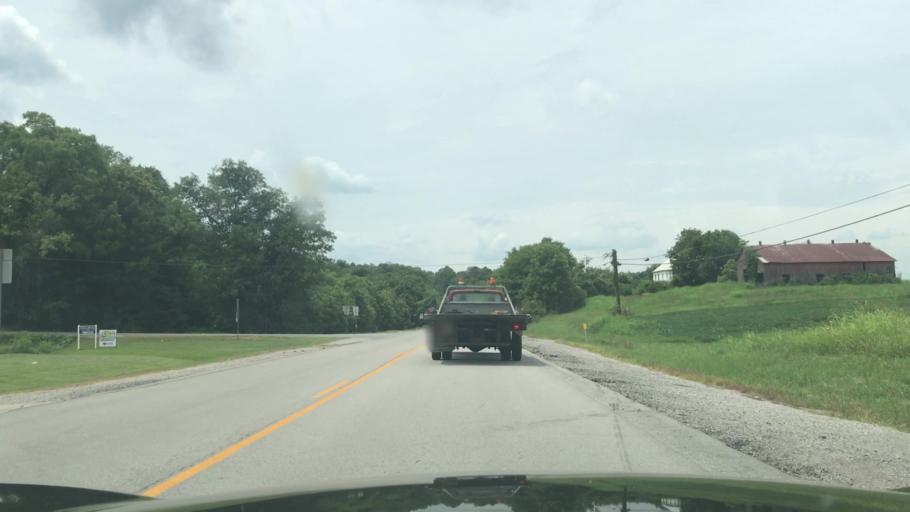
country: US
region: Kentucky
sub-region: Green County
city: Greensburg
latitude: 37.2653
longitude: -85.5867
